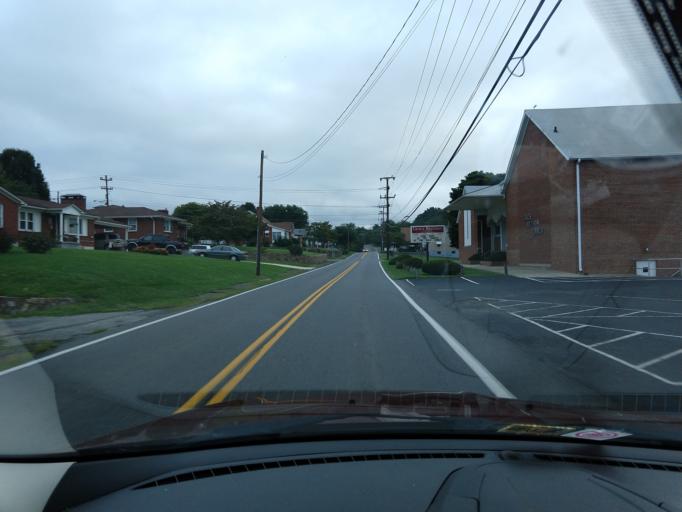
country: US
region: Virginia
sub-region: City of Covington
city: Fairlawn
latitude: 37.7584
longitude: -79.9874
